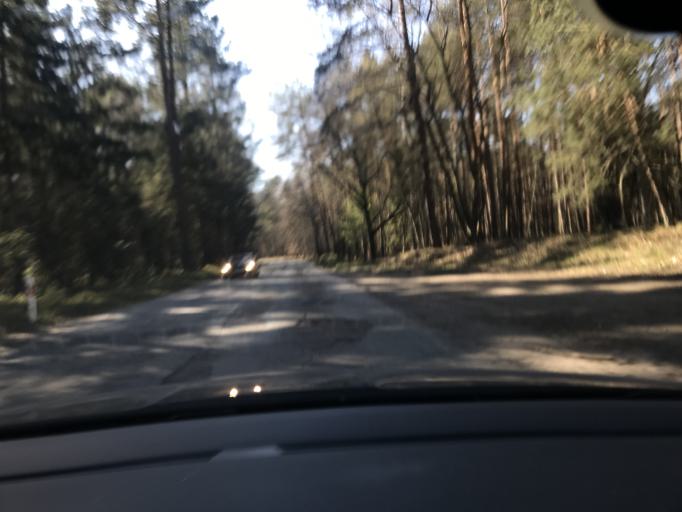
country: PL
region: Pomeranian Voivodeship
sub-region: Powiat nowodworski
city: Krynica Morska
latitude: 54.3564
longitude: 19.3238
